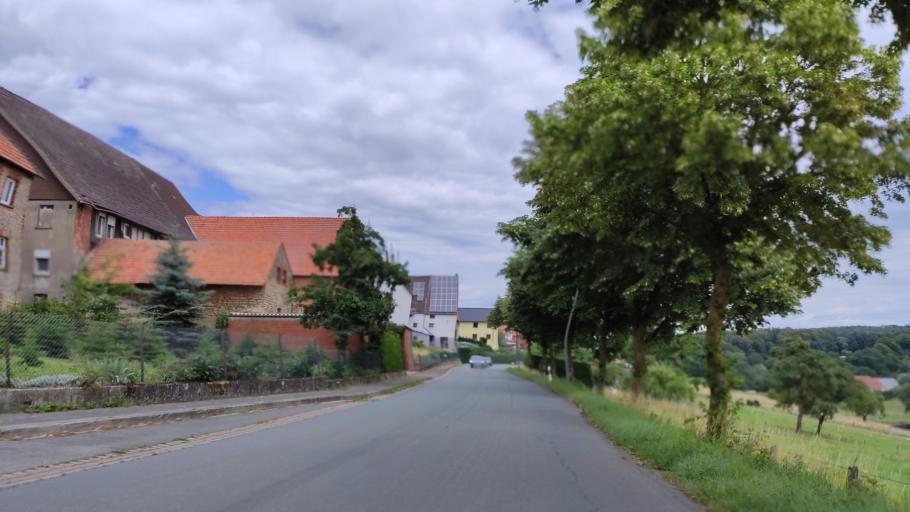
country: DE
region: North Rhine-Westphalia
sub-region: Regierungsbezirk Detmold
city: Nieheim
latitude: 51.7730
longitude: 9.0722
